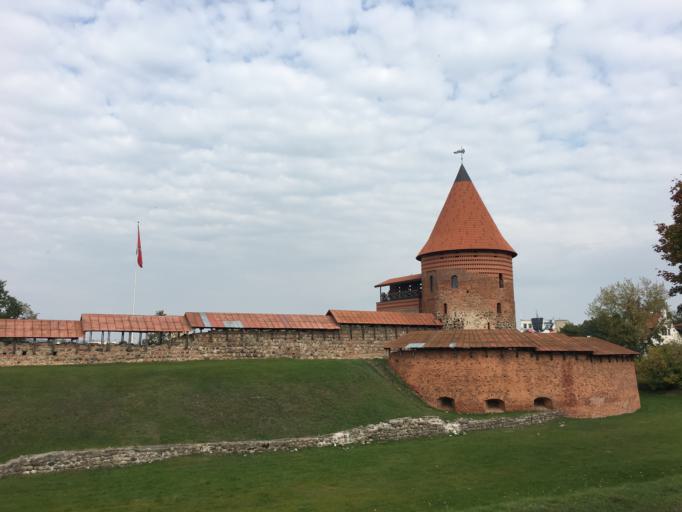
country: LT
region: Kauno apskritis
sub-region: Kaunas
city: Kaunas
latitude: 54.8982
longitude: 23.8844
